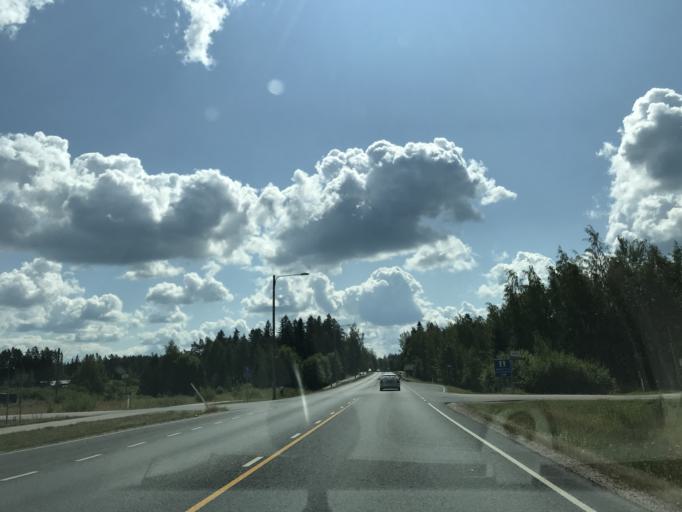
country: FI
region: Paijanne Tavastia
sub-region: Lahti
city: Orimattila
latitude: 60.8227
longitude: 25.7290
